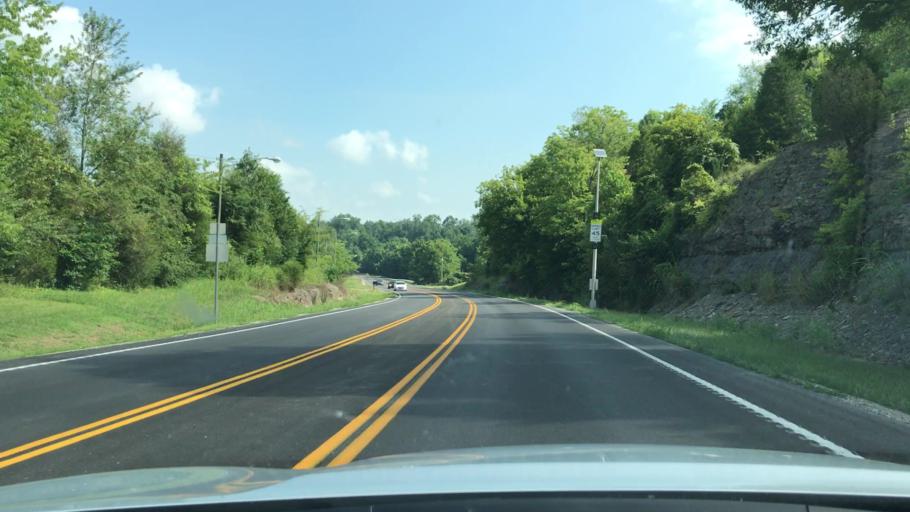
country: US
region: Kentucky
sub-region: Barren County
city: Glasgow
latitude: 37.0198
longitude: -85.9062
